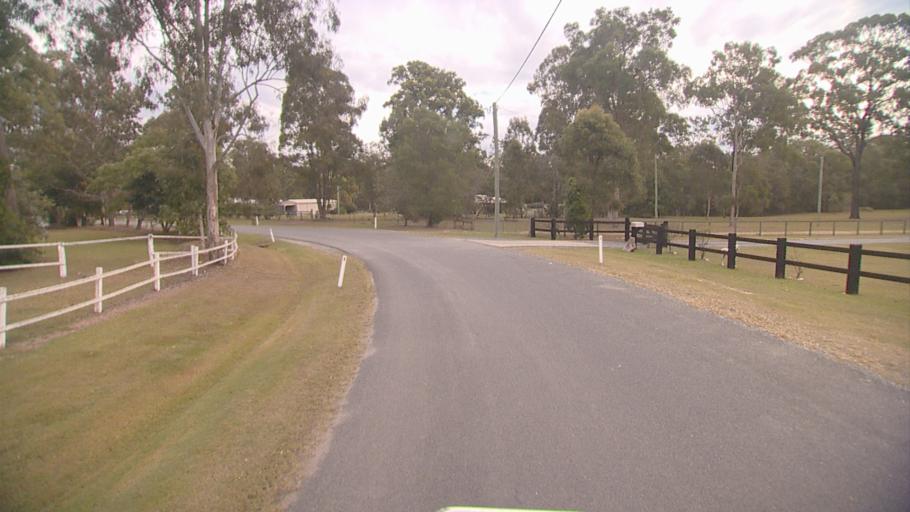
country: AU
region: Queensland
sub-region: Logan
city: Chambers Flat
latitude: -27.7996
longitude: 153.1290
